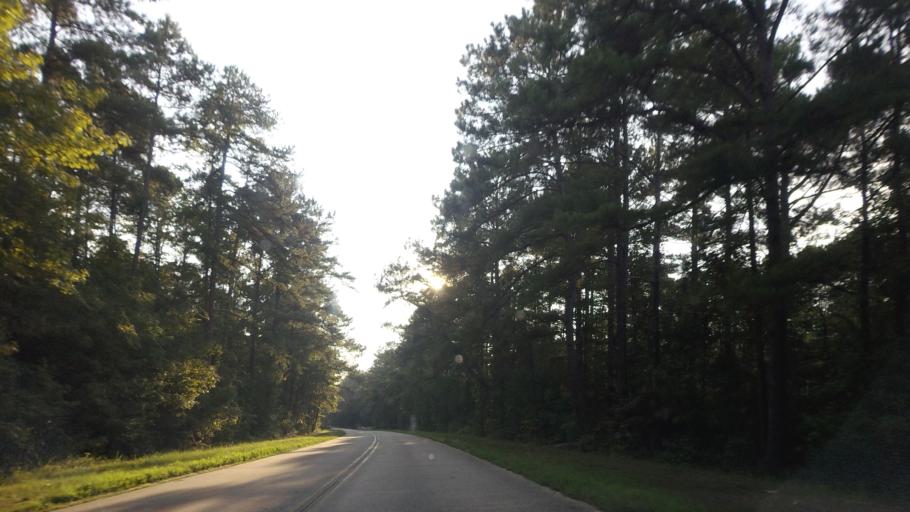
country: US
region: Georgia
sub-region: Bibb County
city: Macon
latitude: 32.9428
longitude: -83.7490
